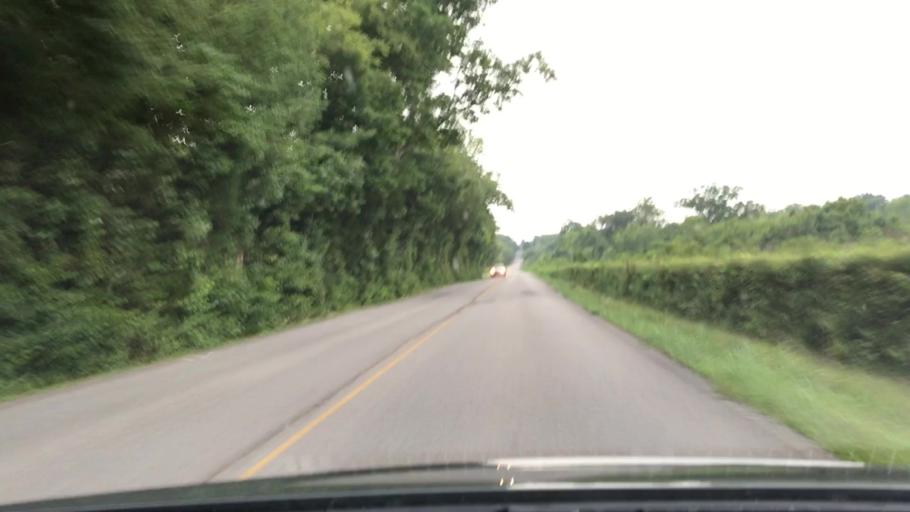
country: US
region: Tennessee
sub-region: Williamson County
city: Nolensville
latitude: 35.9645
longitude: -86.6336
